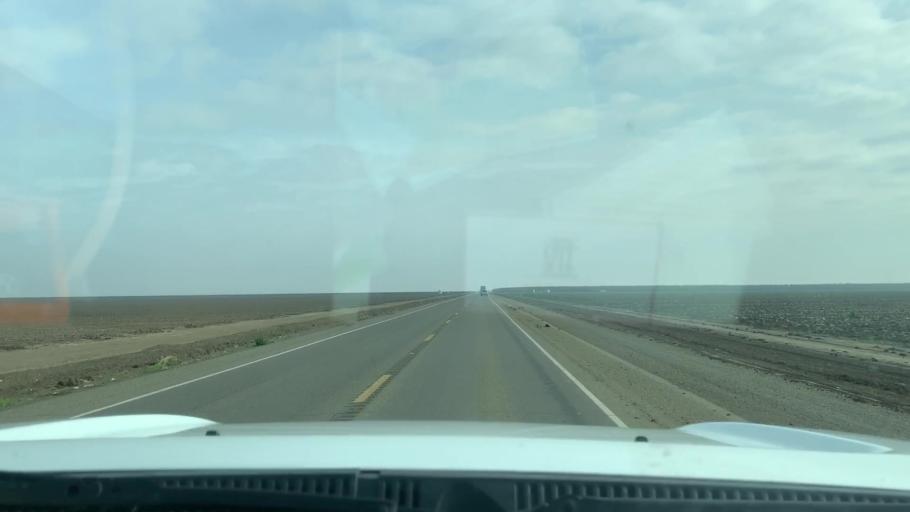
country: US
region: California
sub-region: Fresno County
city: Huron
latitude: 36.2554
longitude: -120.0205
